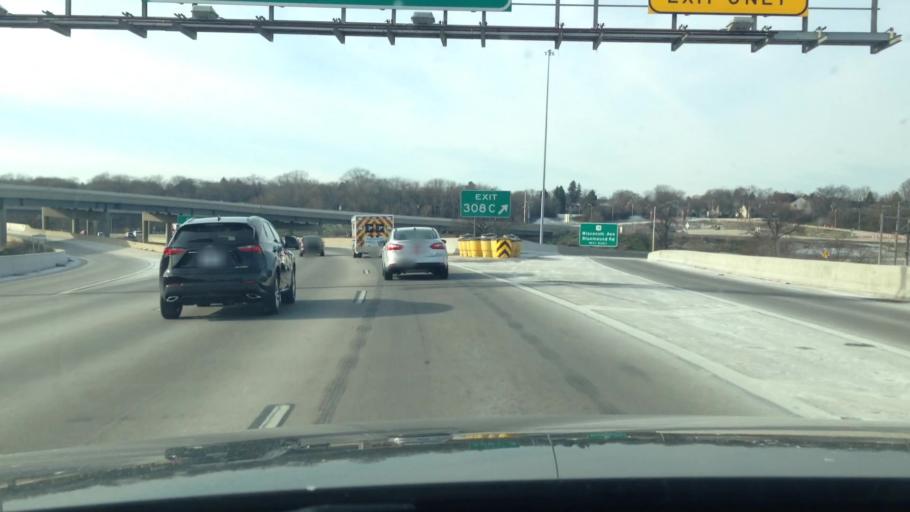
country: US
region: Wisconsin
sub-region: Milwaukee County
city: West Milwaukee
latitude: 43.0335
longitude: -87.9677
